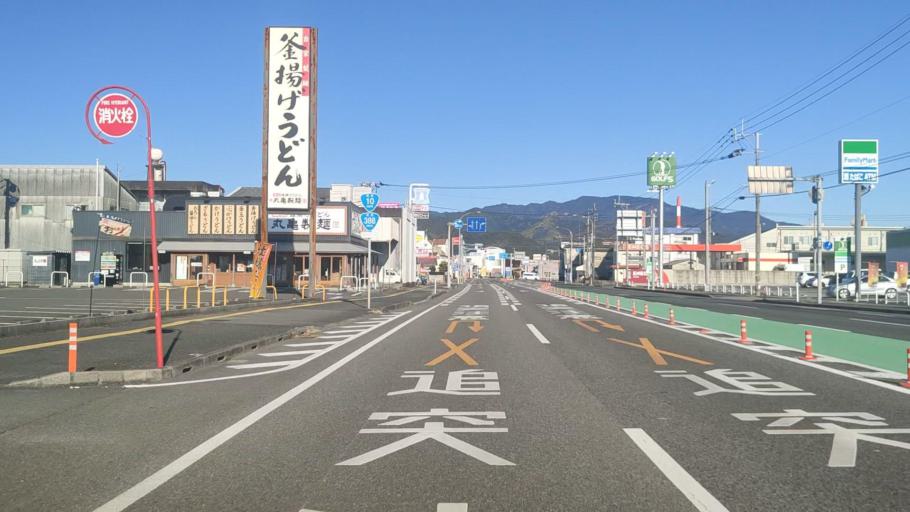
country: JP
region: Miyazaki
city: Nobeoka
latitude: 32.5879
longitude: 131.6766
